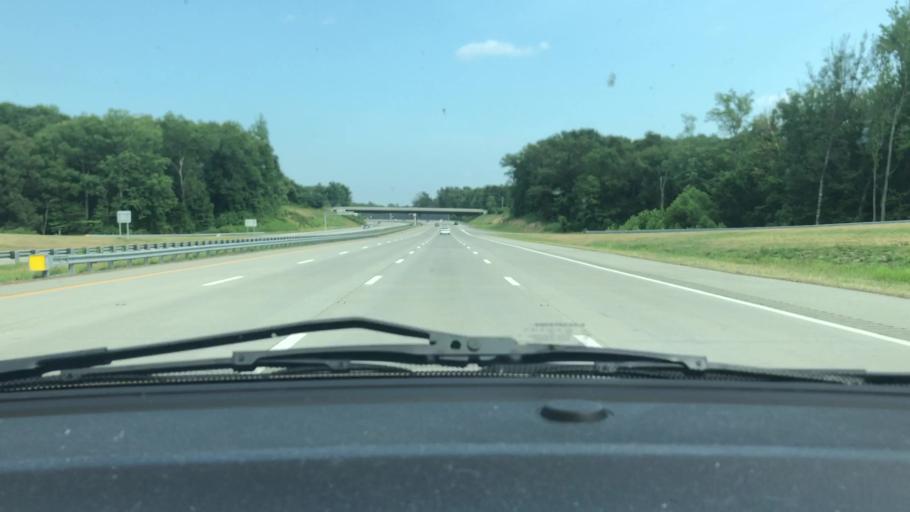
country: US
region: North Carolina
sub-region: Guilford County
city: Jamestown
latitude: 36.0255
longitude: -79.8821
